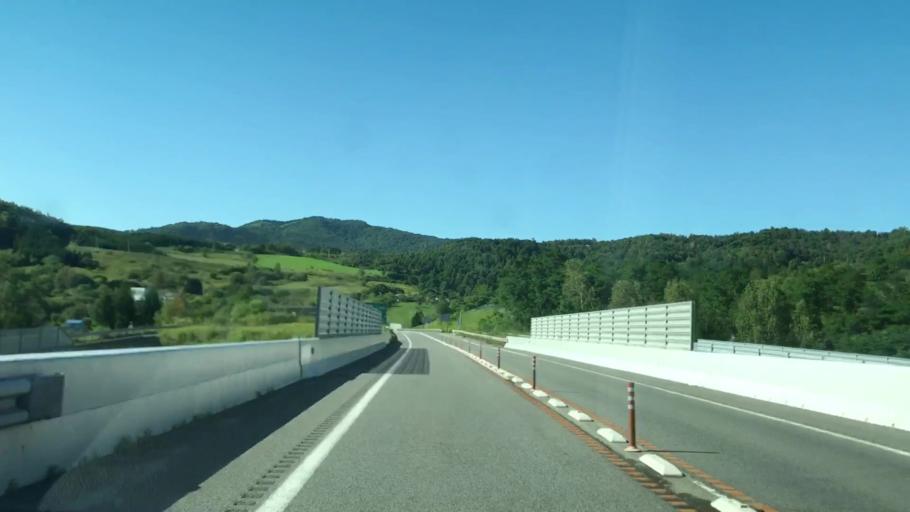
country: JP
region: Hokkaido
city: Date
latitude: 42.5476
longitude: 140.7918
